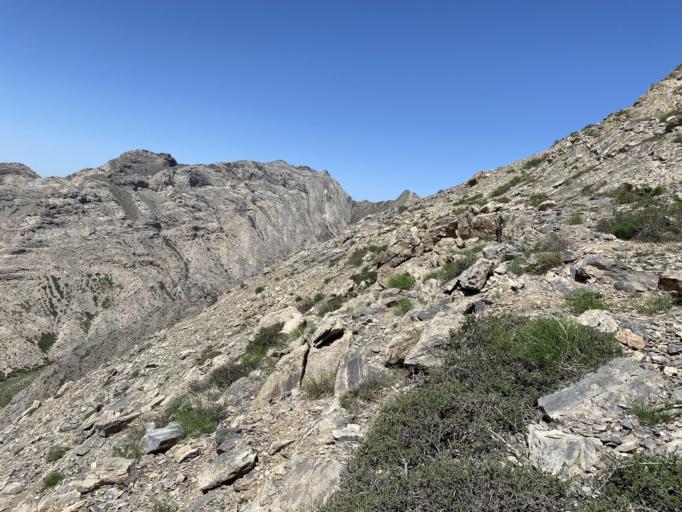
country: KZ
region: Ongtustik Qazaqstan
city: Kentau
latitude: 43.9547
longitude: 68.2635
